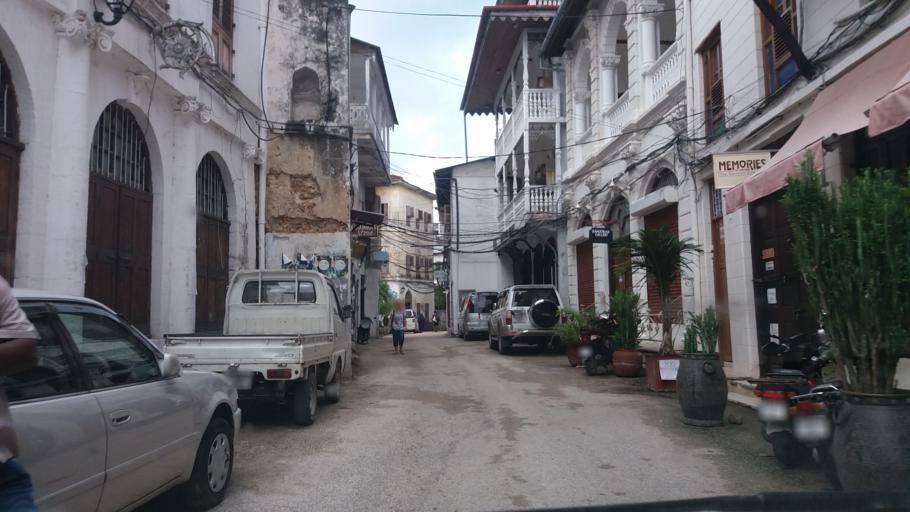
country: TZ
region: Zanzibar Urban/West
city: Zanzibar
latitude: -6.1627
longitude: 39.1877
